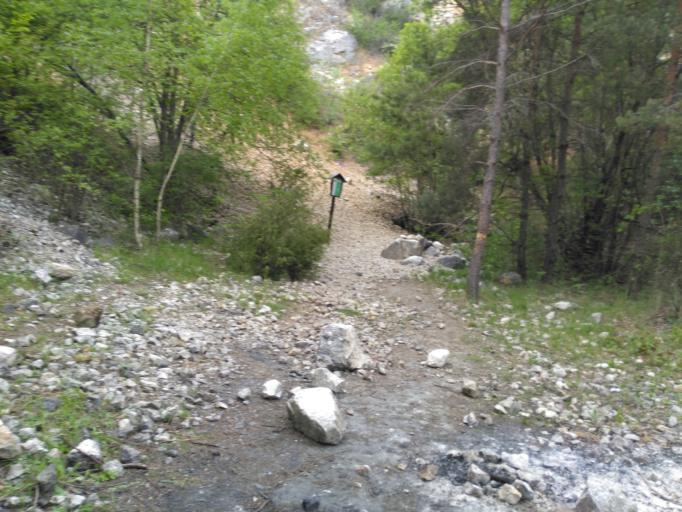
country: CZ
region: Central Bohemia
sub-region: Okres Beroun
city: Kraluv Dvur
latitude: 49.9143
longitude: 14.0652
